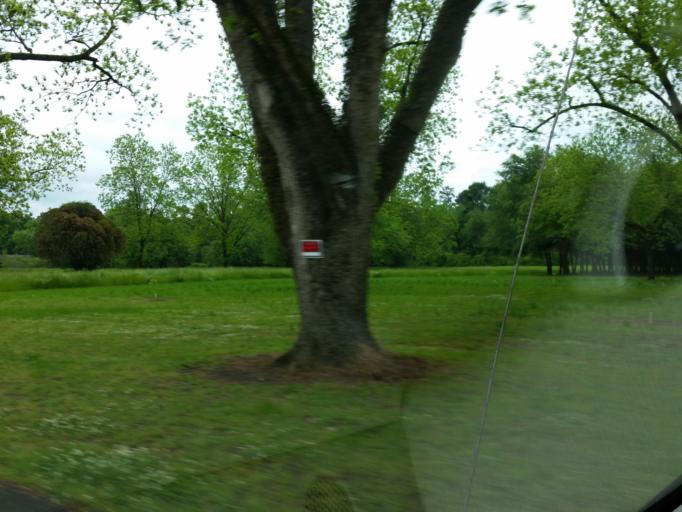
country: US
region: Georgia
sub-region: Peach County
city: Byron
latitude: 32.6517
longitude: -83.7743
